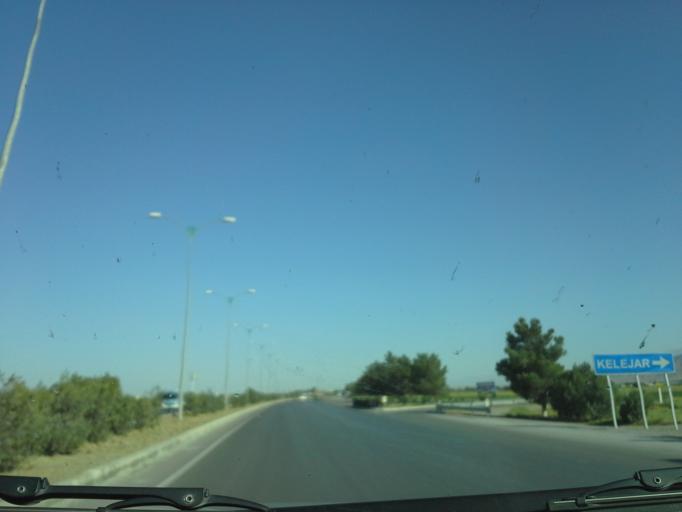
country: TM
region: Ahal
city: Abadan
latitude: 38.1136
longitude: 58.0555
